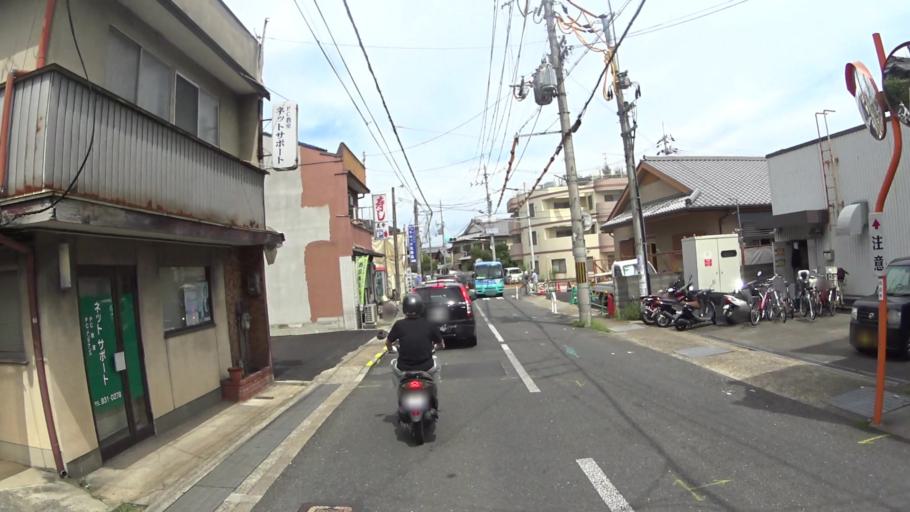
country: JP
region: Kyoto
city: Muko
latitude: 34.9532
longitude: 135.6992
